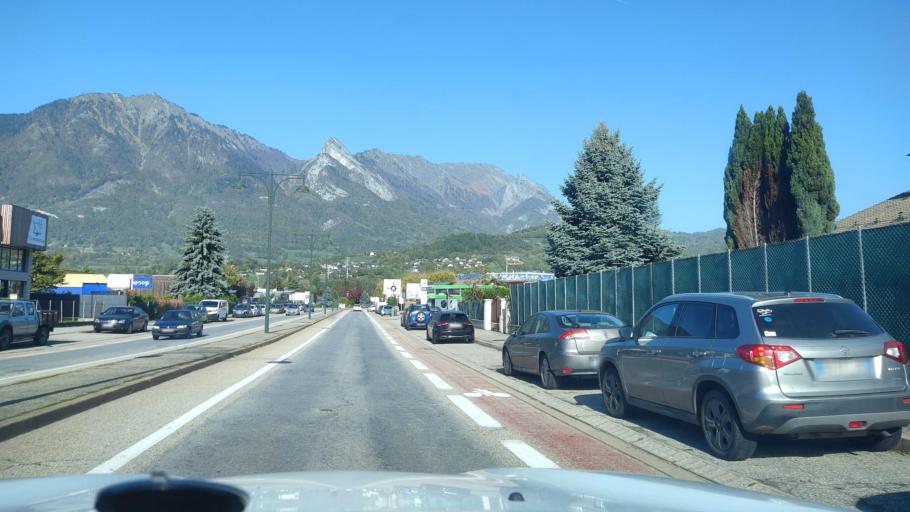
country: FR
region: Rhone-Alpes
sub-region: Departement de la Savoie
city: Grignon
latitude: 45.6595
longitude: 6.3748
